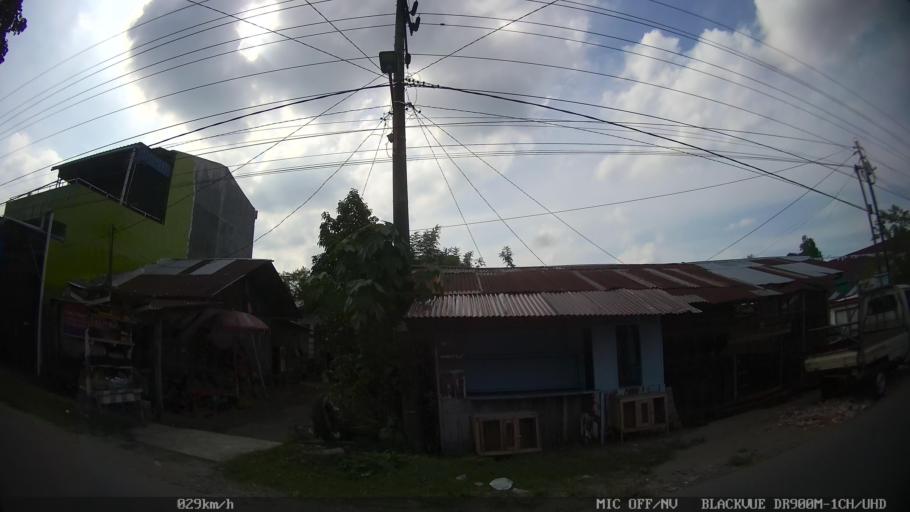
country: ID
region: North Sumatra
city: Binjai
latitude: 3.6357
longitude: 98.4902
